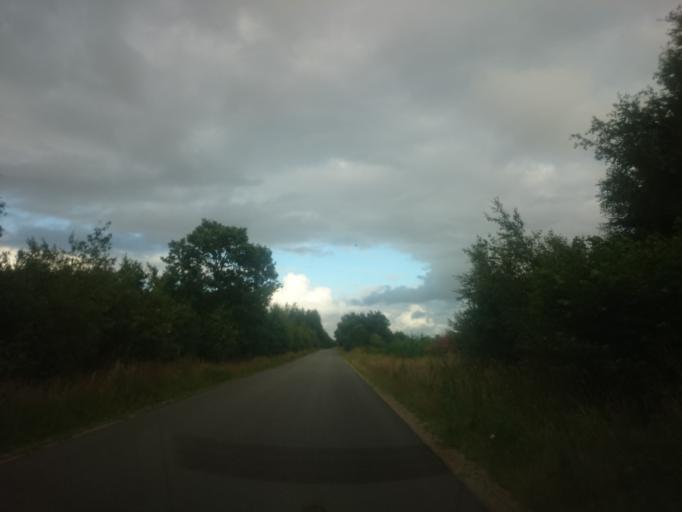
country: DK
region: South Denmark
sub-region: Billund Kommune
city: Grindsted
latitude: 55.6465
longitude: 8.8587
